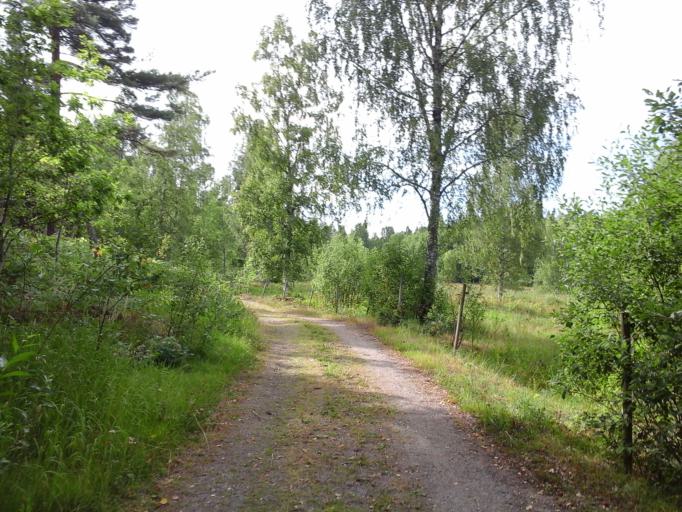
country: SE
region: Soedermanland
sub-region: Eskilstuna Kommun
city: Arla
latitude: 59.2452
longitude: 16.7733
